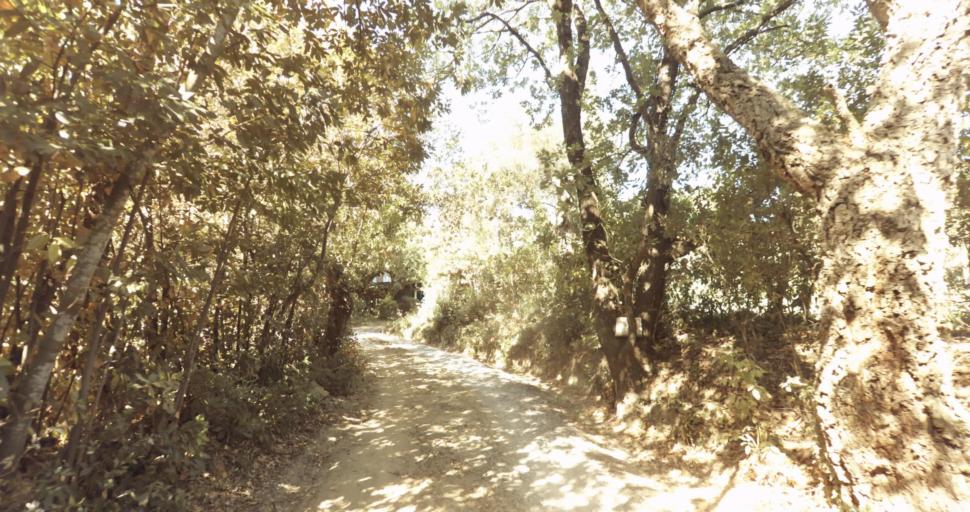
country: FR
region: Provence-Alpes-Cote d'Azur
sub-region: Departement du Var
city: Saint-Tropez
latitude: 43.2583
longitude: 6.6164
